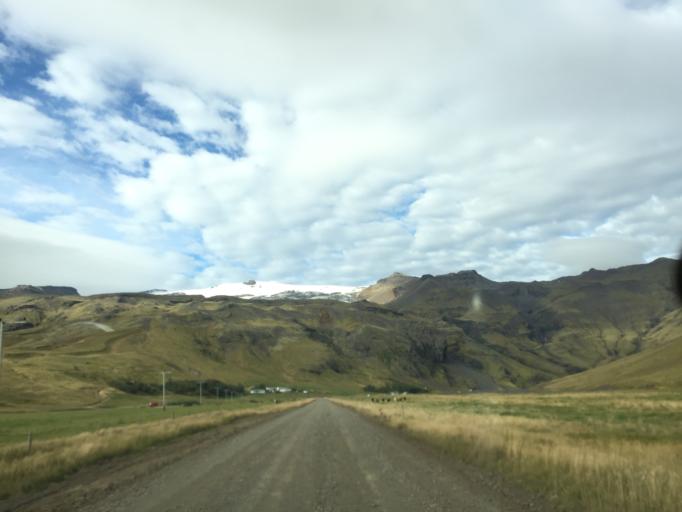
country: IS
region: South
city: Vestmannaeyjar
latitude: 63.5516
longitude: -19.6270
